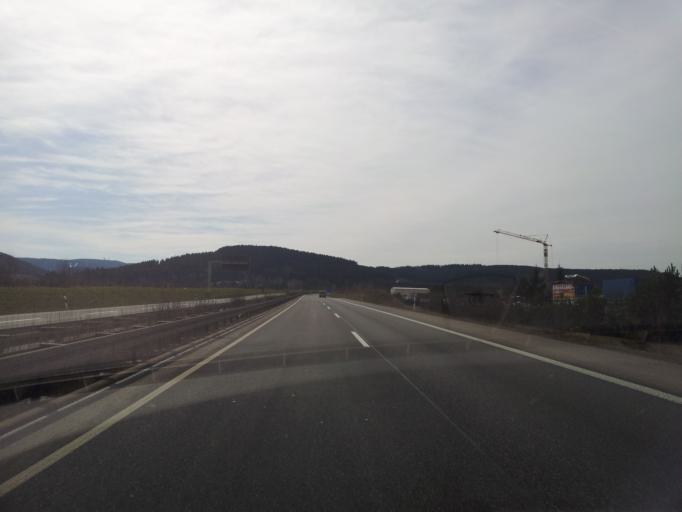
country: DE
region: Thuringia
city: Geraberg
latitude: 50.7230
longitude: 10.8340
